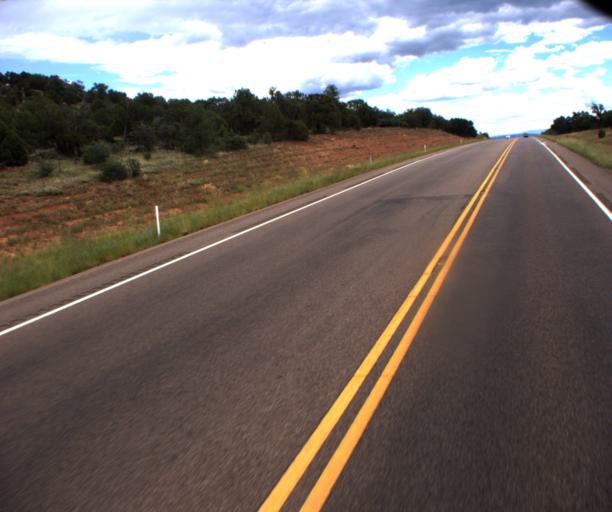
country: US
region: Arizona
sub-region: Navajo County
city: Linden
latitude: 34.2971
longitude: -110.1907
